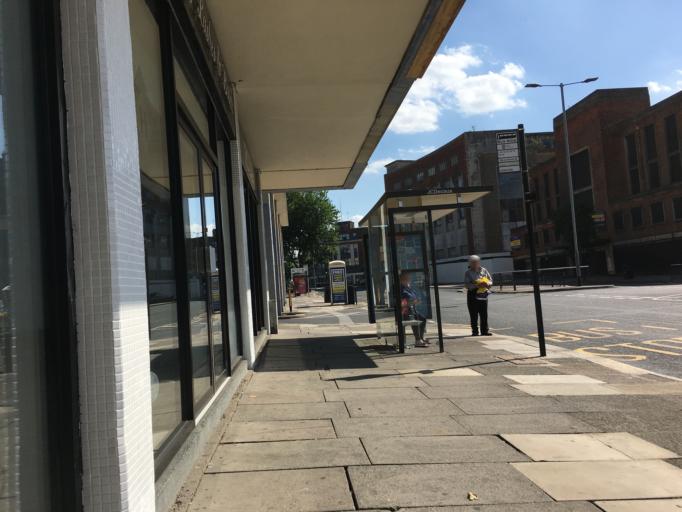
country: GB
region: England
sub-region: City of Kingston upon Hull
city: Hull
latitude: 53.7465
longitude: -0.3394
